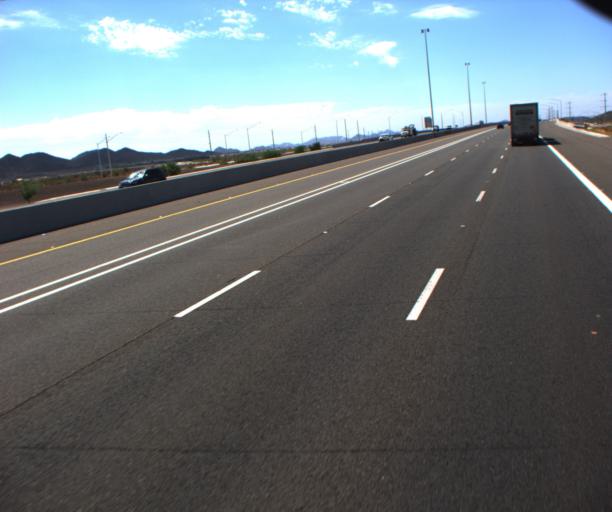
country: US
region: Arizona
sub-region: Maricopa County
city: Anthem
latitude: 33.7741
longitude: -112.1305
